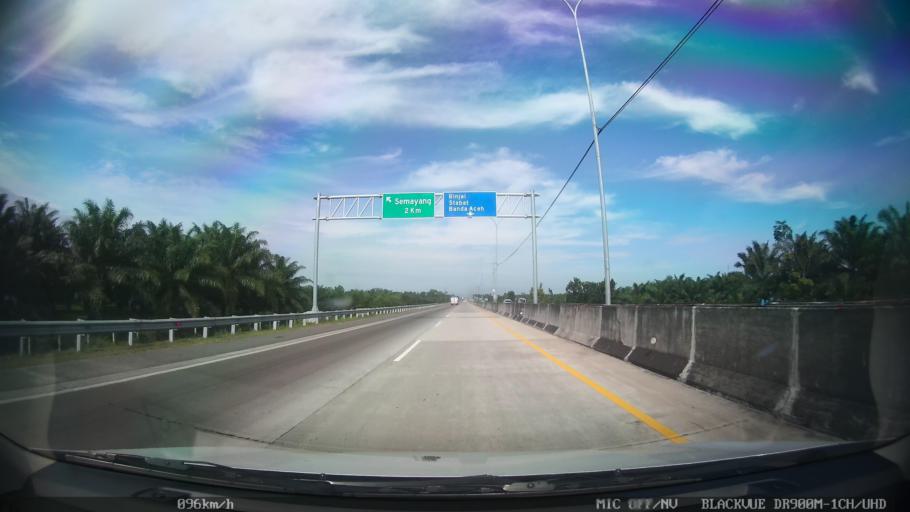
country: ID
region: North Sumatra
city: Sunggal
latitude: 3.6381
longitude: 98.6025
